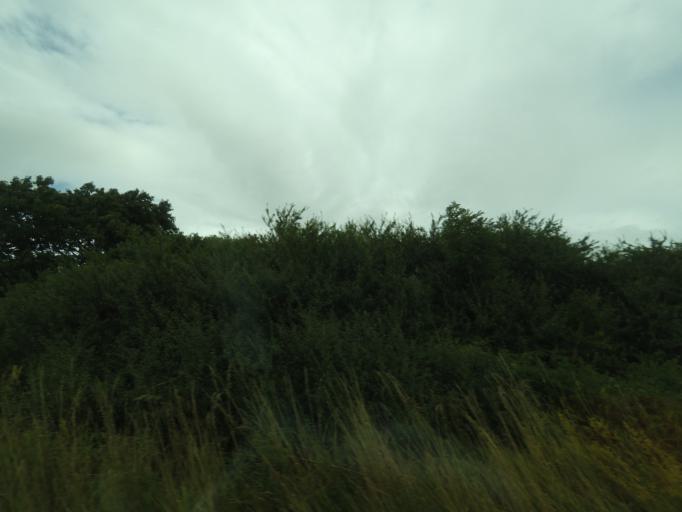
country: DK
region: South Denmark
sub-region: Nordfyns Kommune
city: Sonderso
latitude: 55.4963
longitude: 10.2736
